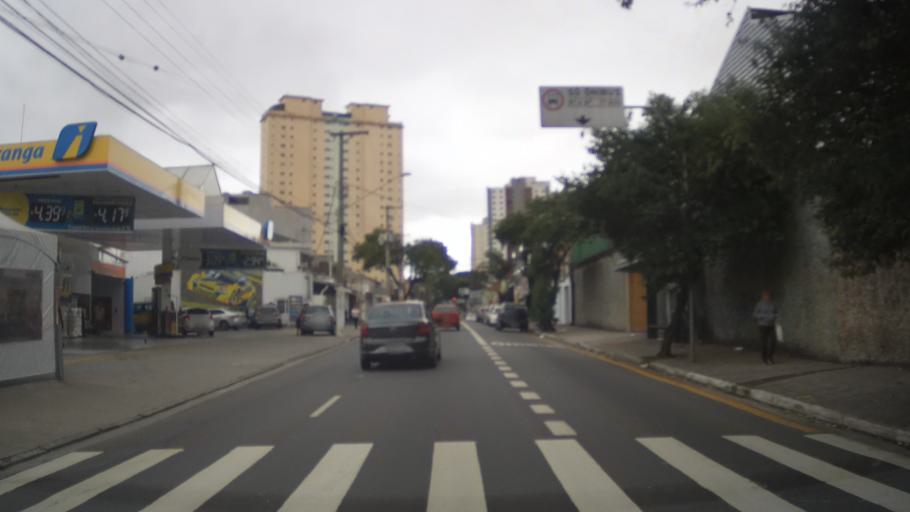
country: BR
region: Sao Paulo
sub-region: Guarulhos
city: Guarulhos
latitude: -23.5275
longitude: -46.5268
